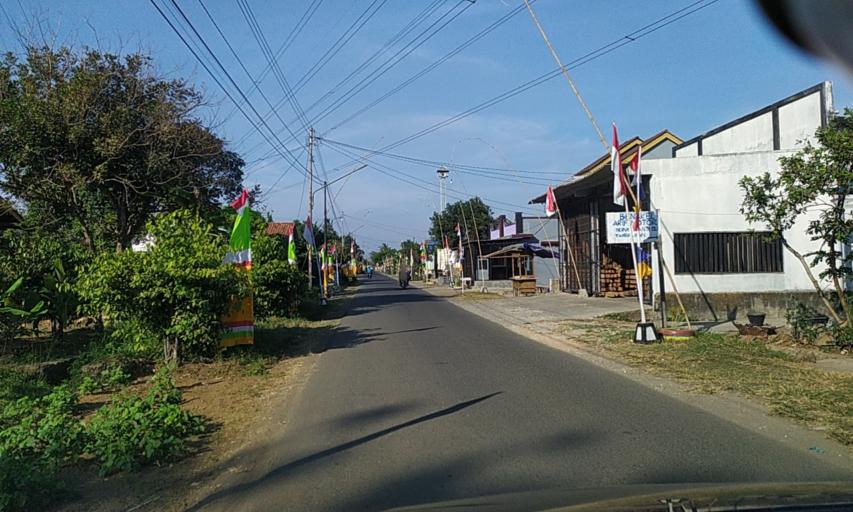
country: ID
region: Central Java
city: Rejanegara
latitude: -7.6759
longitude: 109.0452
